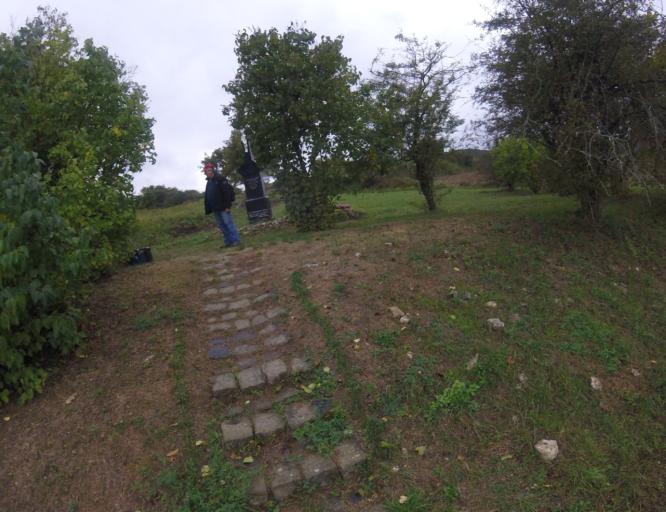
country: HU
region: Pest
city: Szob
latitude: 47.8400
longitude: 18.8674
